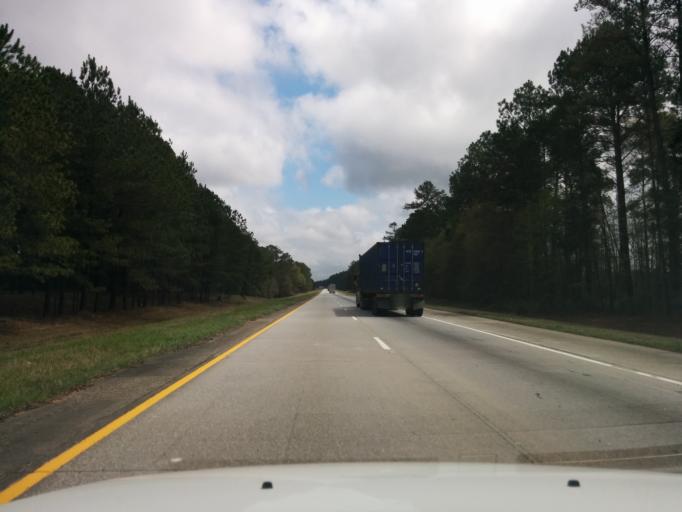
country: US
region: Georgia
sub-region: Emanuel County
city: Swainsboro
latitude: 32.4100
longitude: -82.3611
